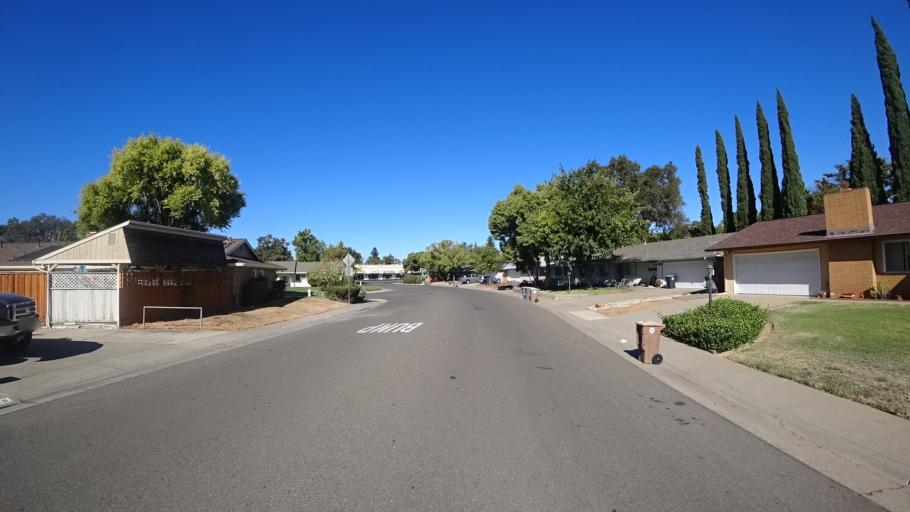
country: US
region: California
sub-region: Sacramento County
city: Elk Grove
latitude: 38.4033
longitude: -121.3701
